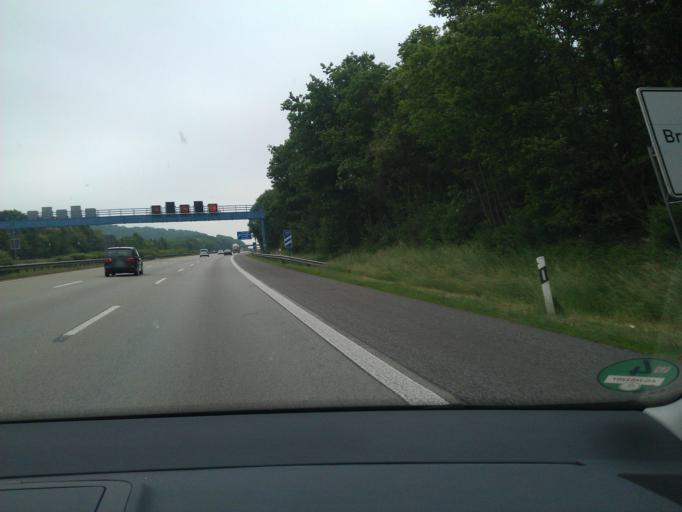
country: DE
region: Rheinland-Pfalz
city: Wehr
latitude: 50.4172
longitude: 7.2337
